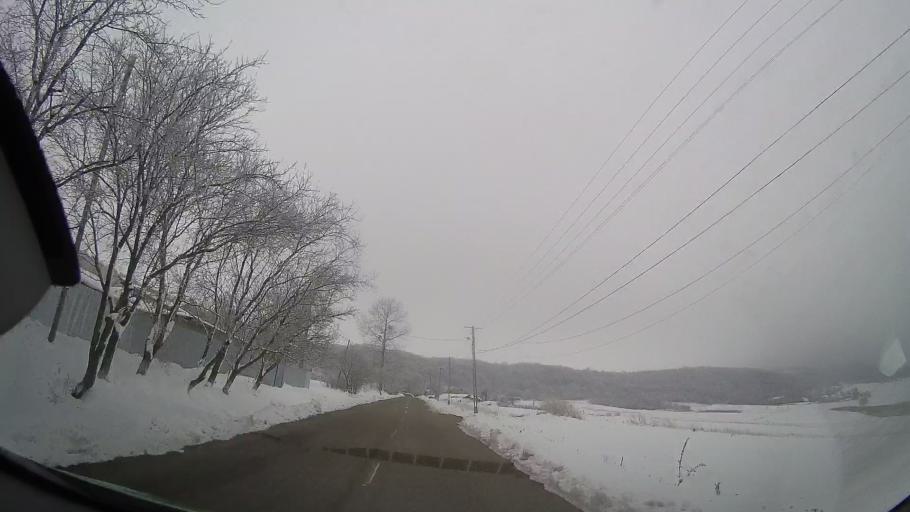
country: RO
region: Neamt
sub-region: Comuna Bozieni
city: Bozieni
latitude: 46.8486
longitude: 27.1720
